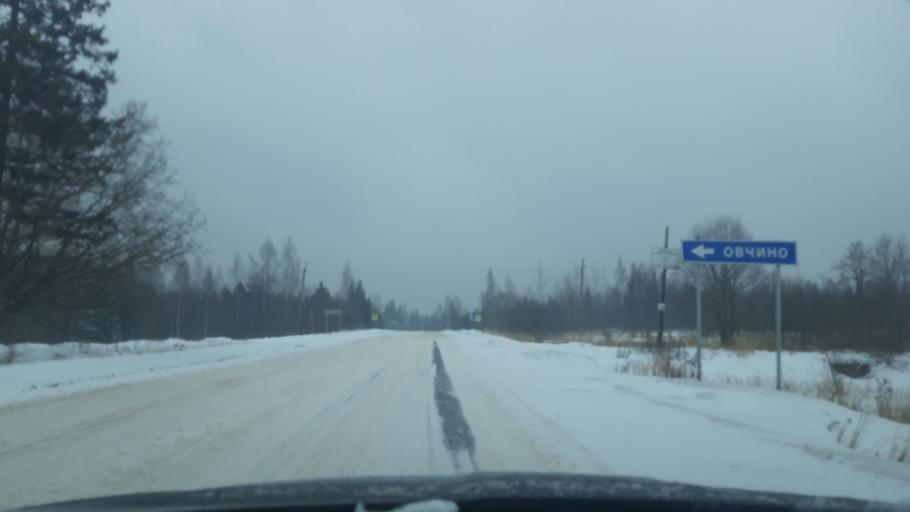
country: RU
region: Moskovskaya
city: Avtopoligon
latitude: 56.2649
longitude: 37.2643
